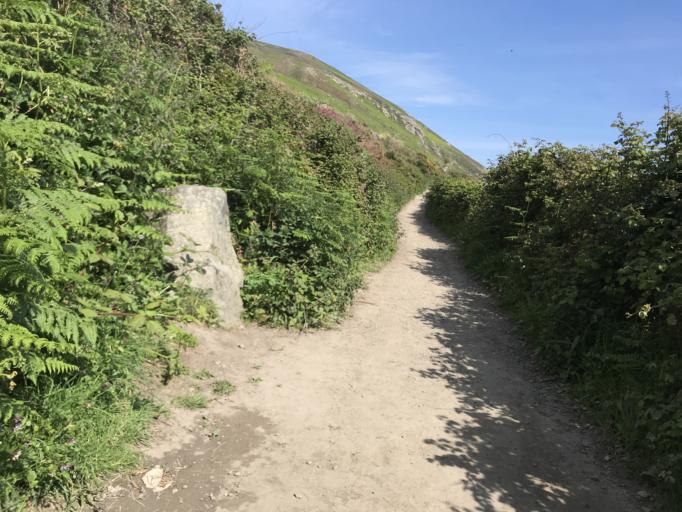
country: IE
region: Leinster
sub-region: Wicklow
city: Bray
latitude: 53.1837
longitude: -6.0777
